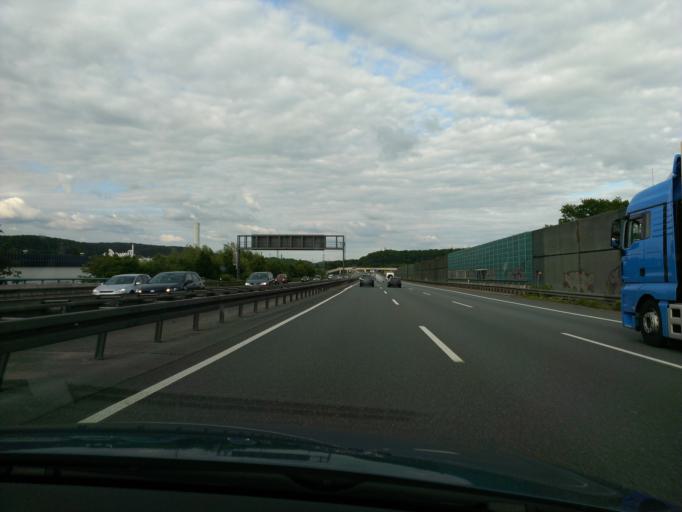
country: DE
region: North Rhine-Westphalia
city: Herdecke
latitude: 51.4058
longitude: 7.4794
